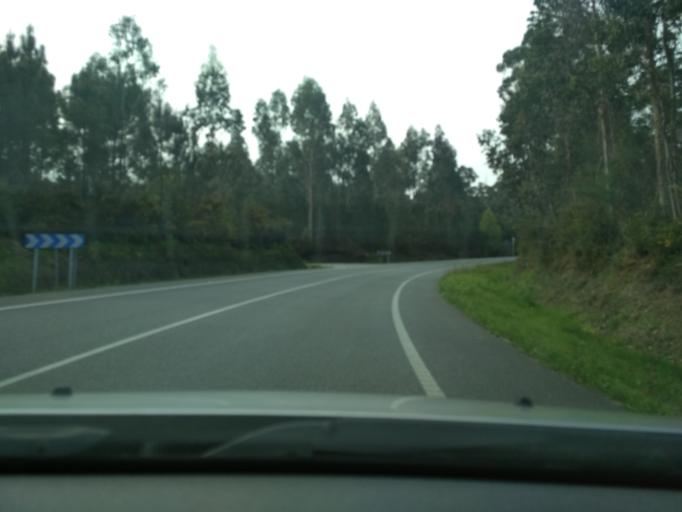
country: ES
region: Galicia
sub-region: Provincia de Pontevedra
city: Catoira
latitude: 42.6577
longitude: -8.7033
